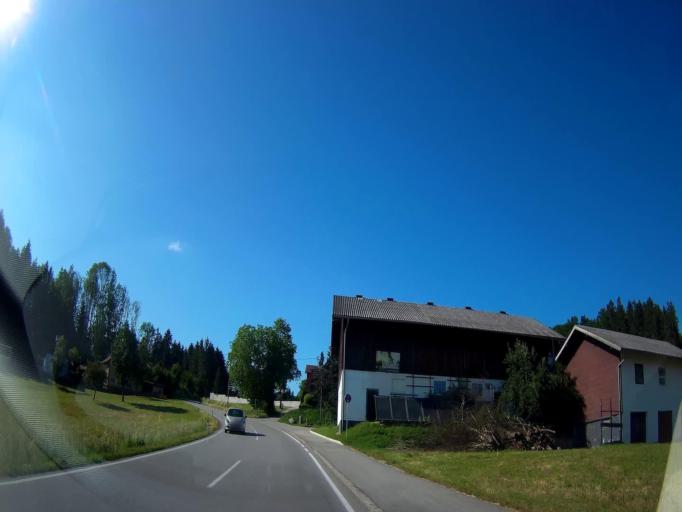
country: AT
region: Salzburg
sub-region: Politischer Bezirk Salzburg-Umgebung
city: Dorfbeuern
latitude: 48.0680
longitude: 12.9891
